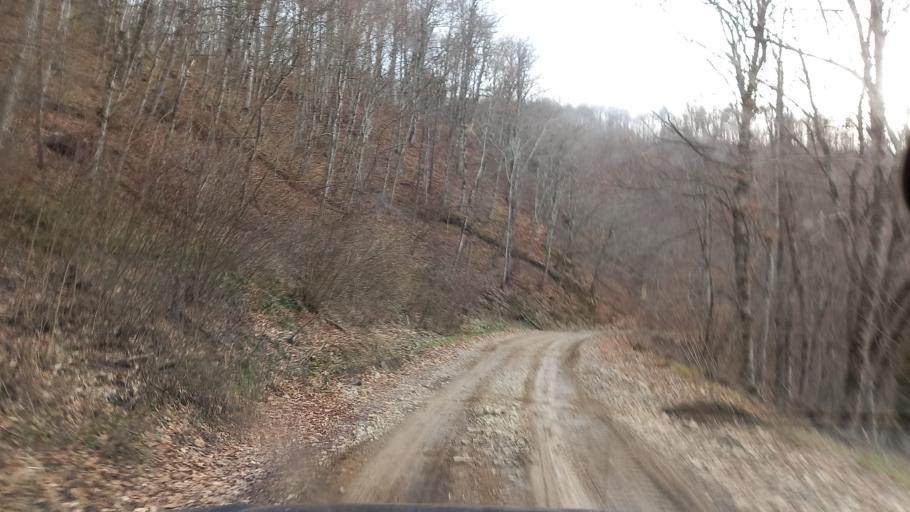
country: RU
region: Adygeya
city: Kamennomostskiy
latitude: 44.1552
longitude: 40.3027
